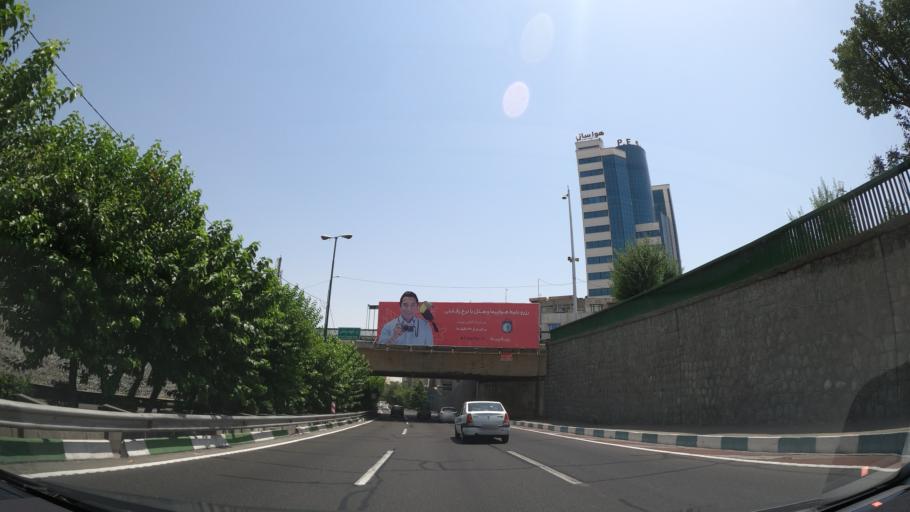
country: IR
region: Tehran
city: Tehran
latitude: 35.7296
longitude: 51.4210
